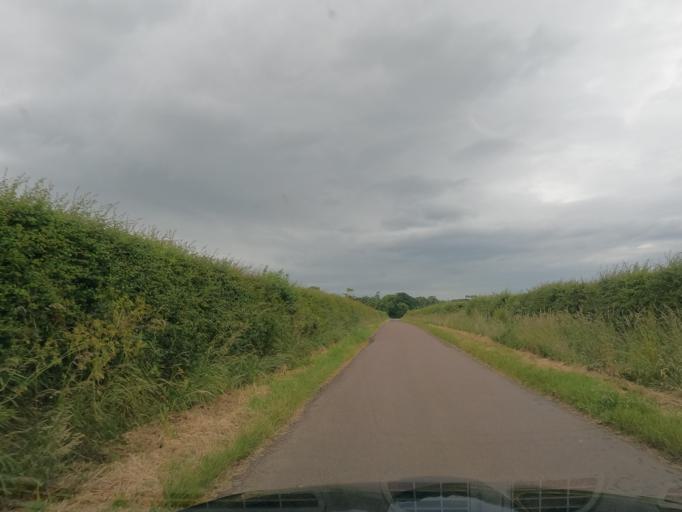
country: GB
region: England
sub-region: Northumberland
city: Ancroft
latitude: 55.6720
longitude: -2.0412
